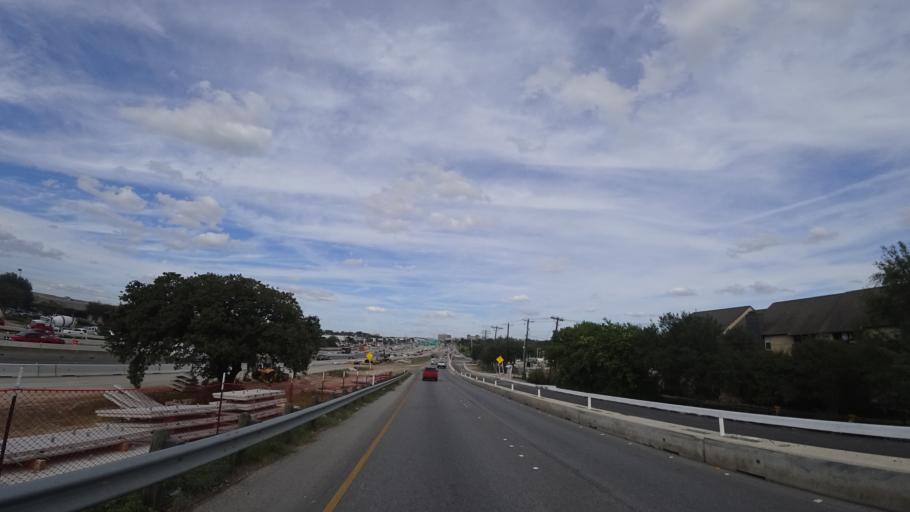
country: US
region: Texas
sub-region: Travis County
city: Onion Creek
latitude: 30.1988
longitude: -97.7631
